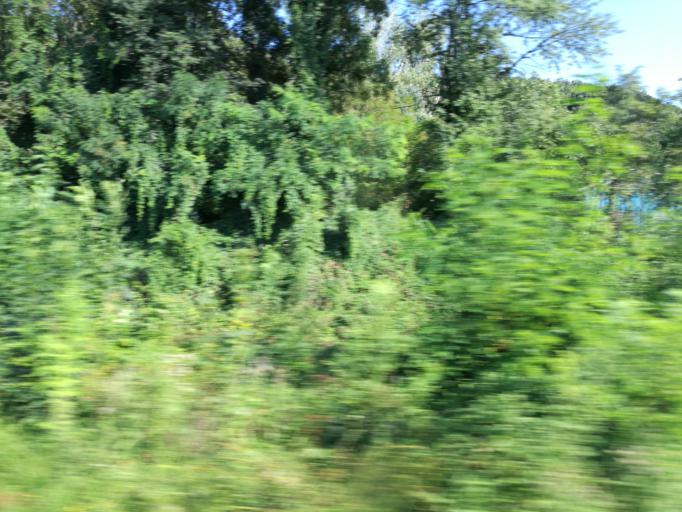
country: RO
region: Iasi
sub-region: Comuna Ciurea
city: Ciurea
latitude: 47.0138
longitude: 27.5708
